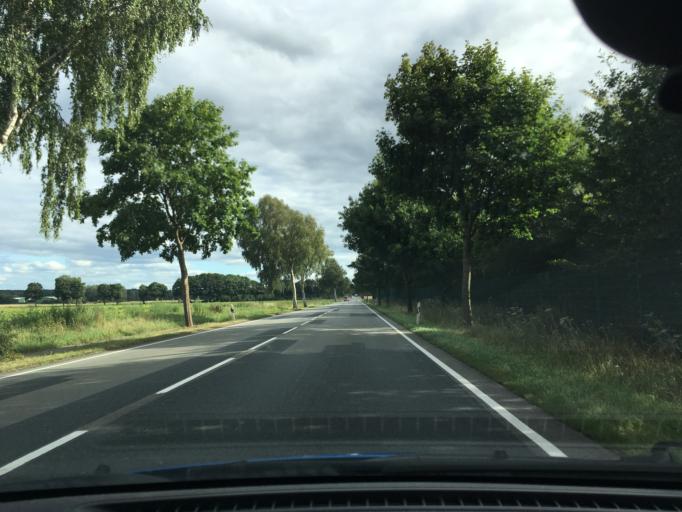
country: DE
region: Lower Saxony
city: Neu Wulmstorf
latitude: 53.4191
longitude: 9.7895
